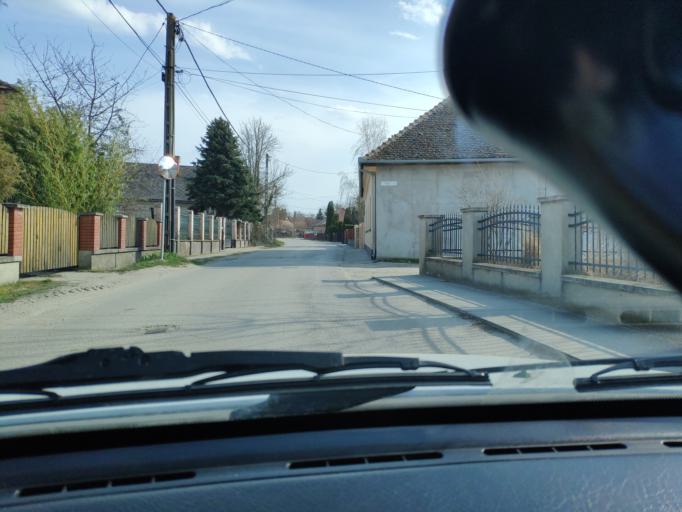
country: HU
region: Pest
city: Rackeve
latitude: 47.1625
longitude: 18.9407
